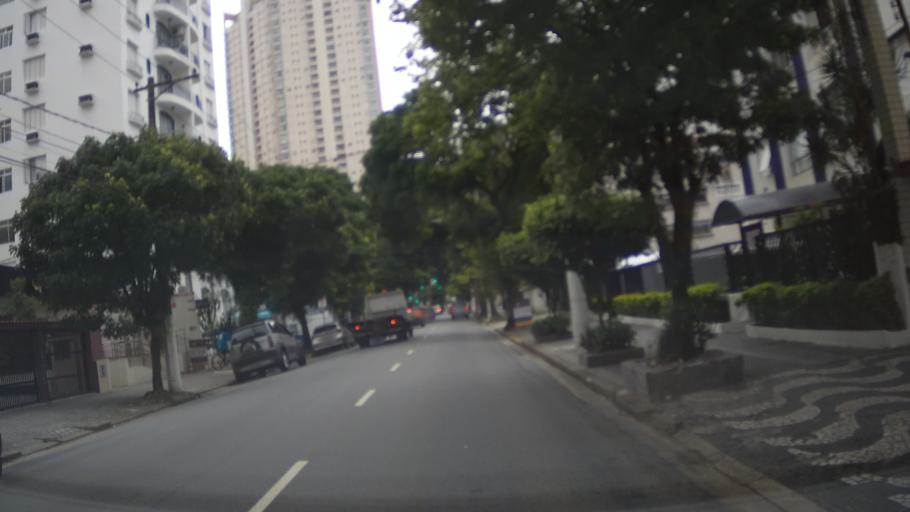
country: BR
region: Sao Paulo
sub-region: Santos
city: Santos
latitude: -23.9718
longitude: -46.3219
